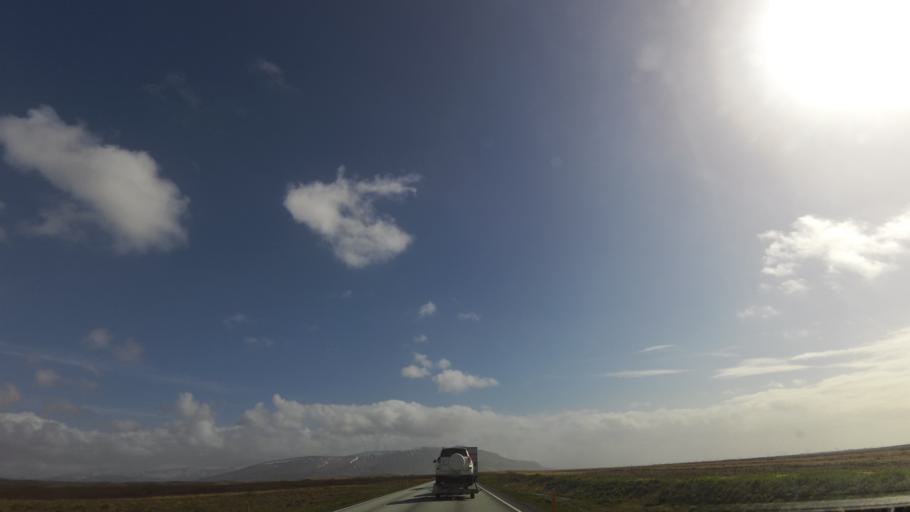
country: IS
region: West
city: Borgarnes
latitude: 64.4398
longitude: -21.9583
